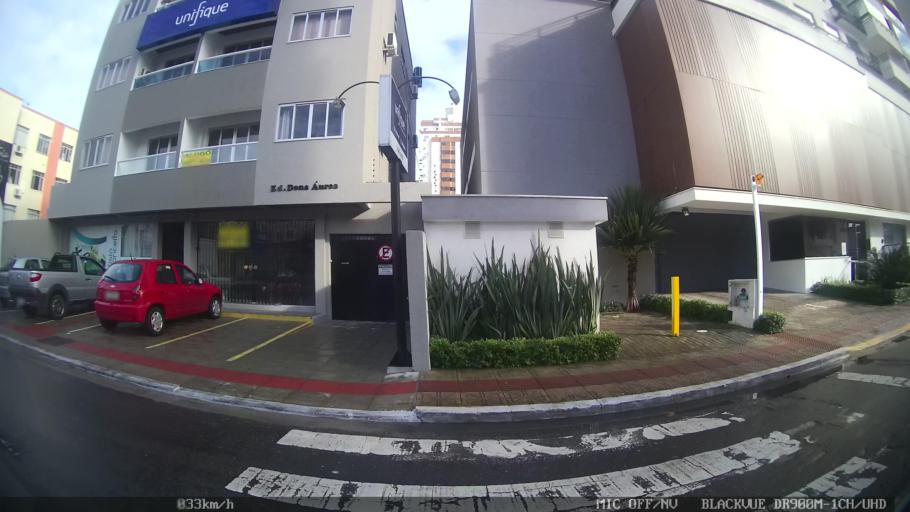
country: BR
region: Santa Catarina
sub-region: Sao Jose
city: Campinas
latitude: -27.5982
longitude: -48.6151
